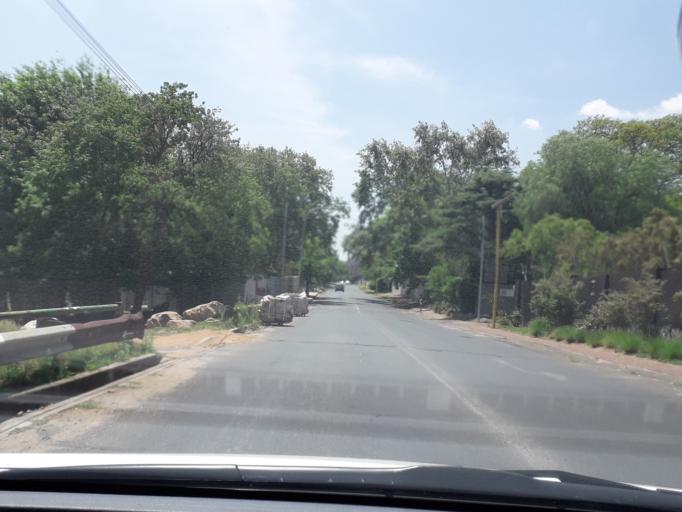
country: ZA
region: Gauteng
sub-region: City of Johannesburg Metropolitan Municipality
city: Johannesburg
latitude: -26.1117
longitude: 28.0207
